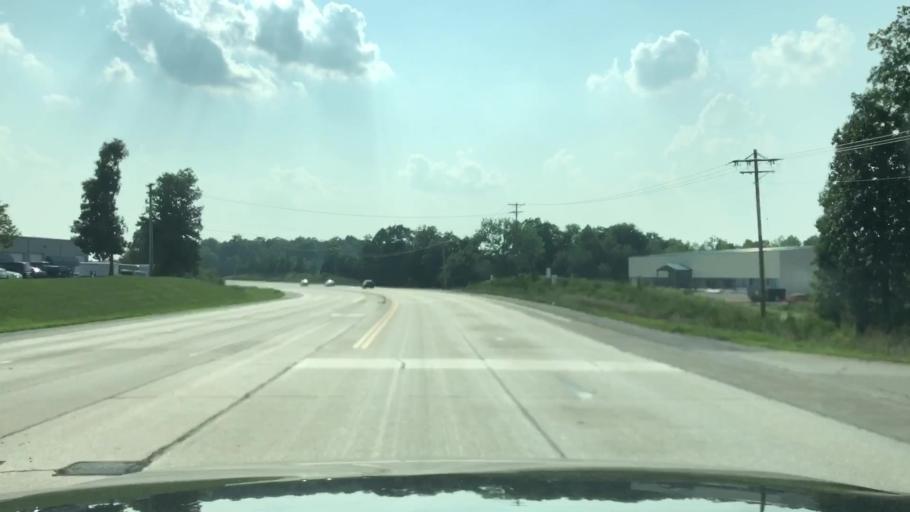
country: US
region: Missouri
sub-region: Saint Charles County
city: Wentzville
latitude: 38.8263
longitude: -90.8435
